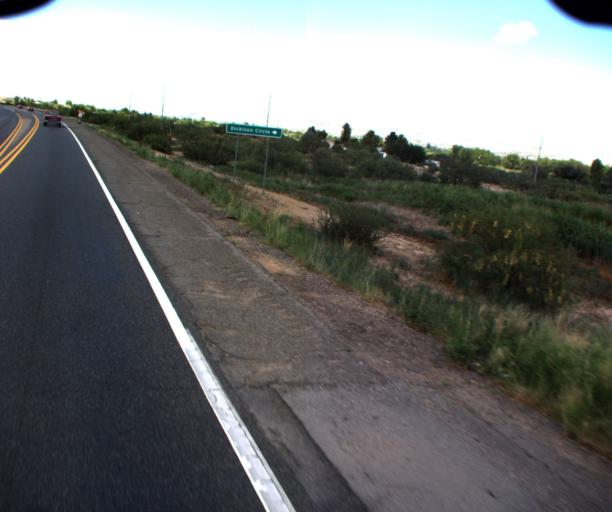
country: US
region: Arizona
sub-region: Yavapai County
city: Camp Verde
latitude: 34.5898
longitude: -111.8881
